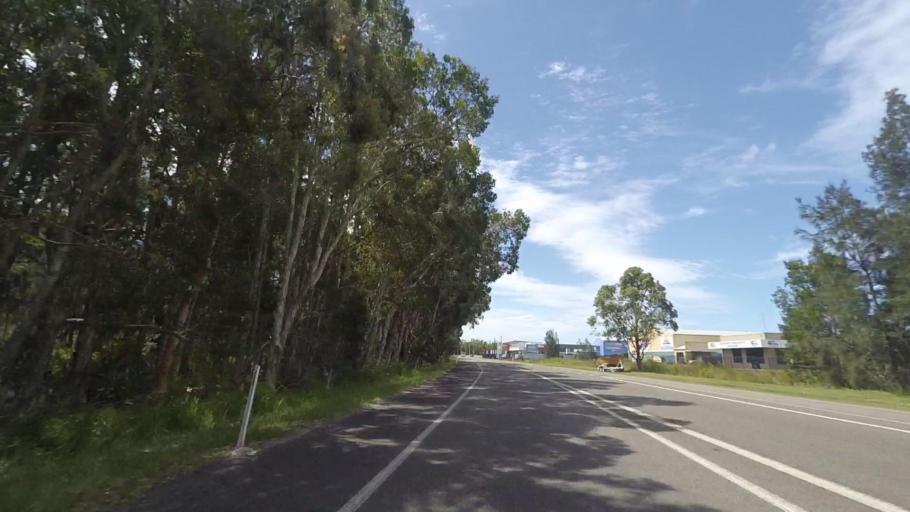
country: AU
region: New South Wales
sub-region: Port Stephens Shire
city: Anna Bay
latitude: -32.7526
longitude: 152.0686
